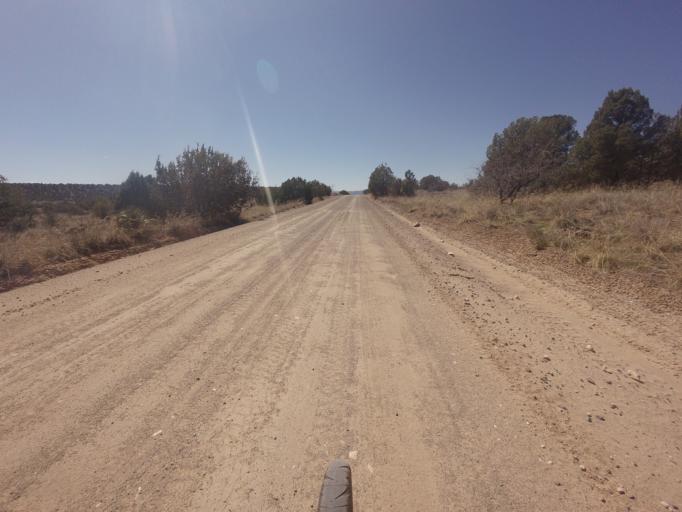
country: US
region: Arizona
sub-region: Yavapai County
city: Lake Montezuma
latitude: 34.5977
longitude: -111.7257
